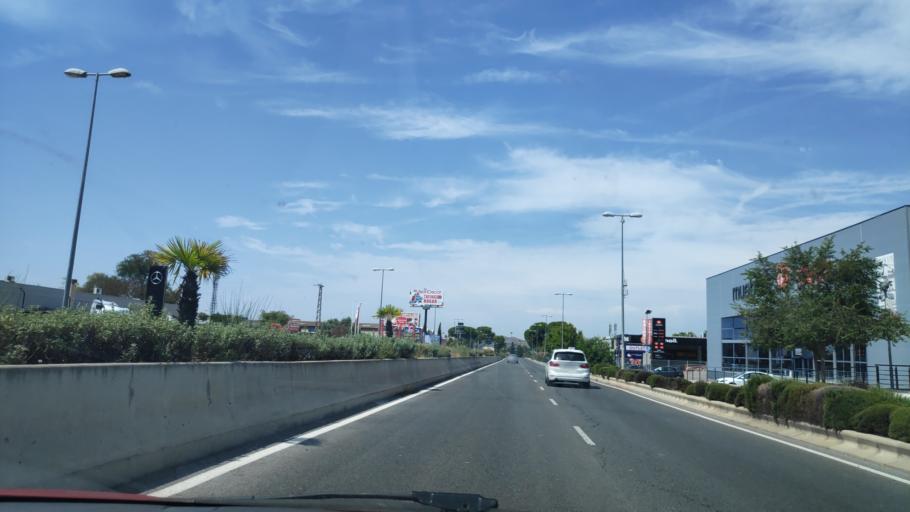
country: ES
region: Madrid
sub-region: Provincia de Madrid
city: Vaciamadrid
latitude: 40.3103
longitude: -3.4814
